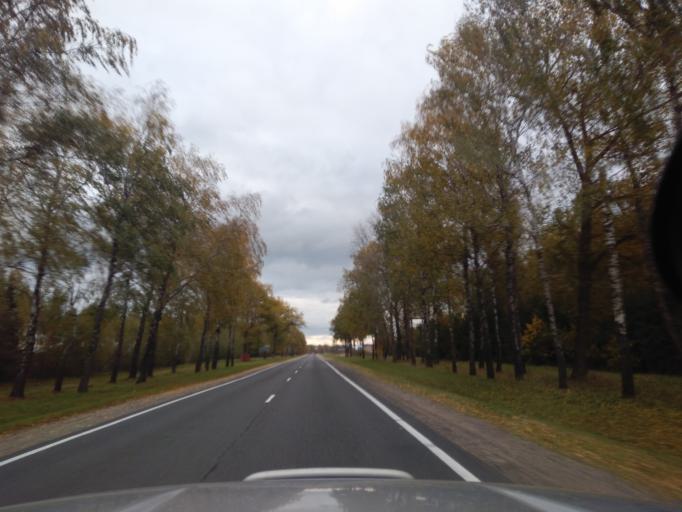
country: BY
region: Minsk
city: Slutsk
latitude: 53.2197
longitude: 27.5353
